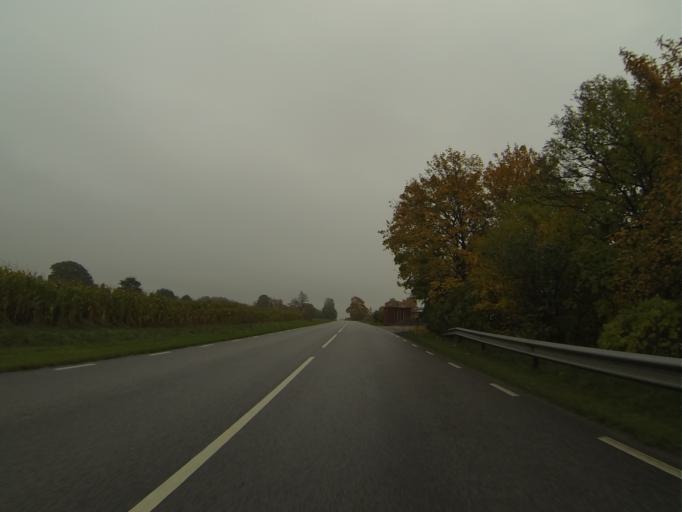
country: SE
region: Skane
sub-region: Hoors Kommun
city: Loberod
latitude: 55.7136
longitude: 13.5365
